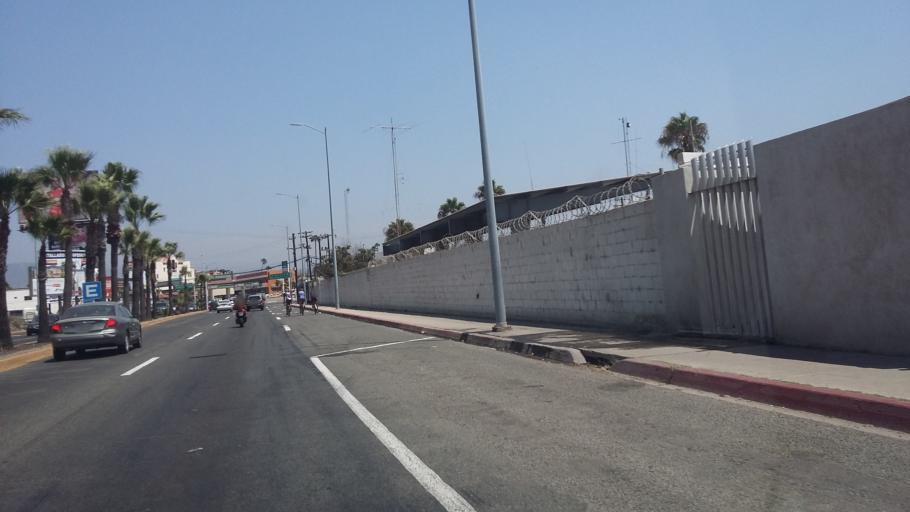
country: MX
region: Baja California
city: Ensenada
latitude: 31.8613
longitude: -116.6315
